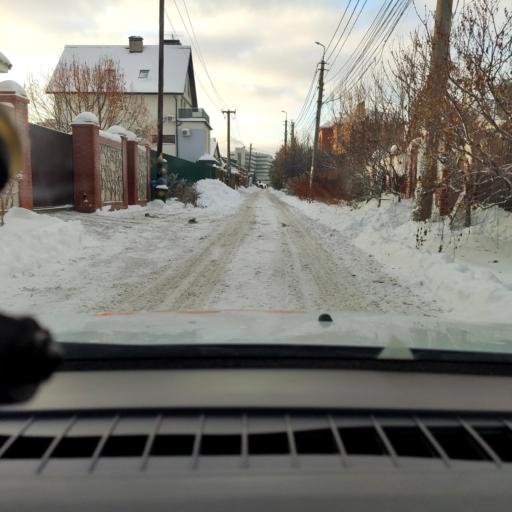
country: RU
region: Samara
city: Samara
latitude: 53.2672
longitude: 50.2109
